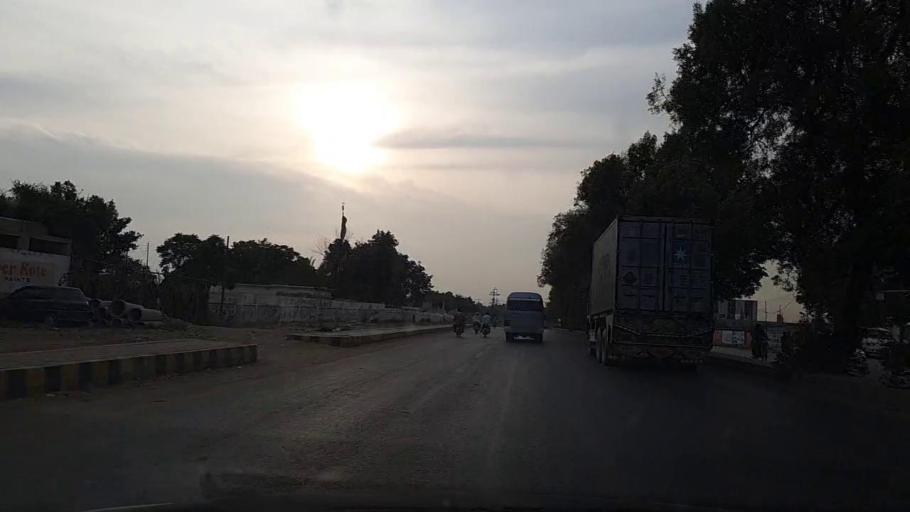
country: PK
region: Sindh
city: Malir Cantonment
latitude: 24.8555
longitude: 67.2565
